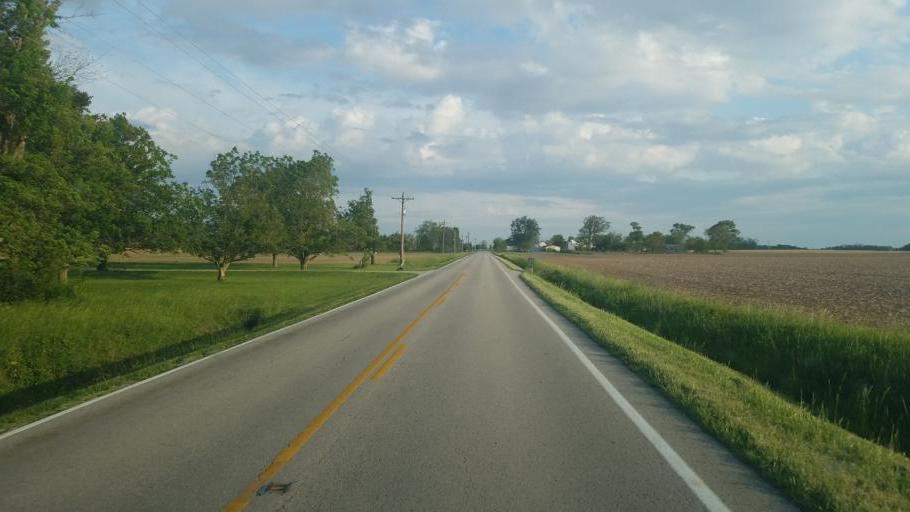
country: US
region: Ohio
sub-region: Highland County
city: Leesburg
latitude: 39.4068
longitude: -83.6060
